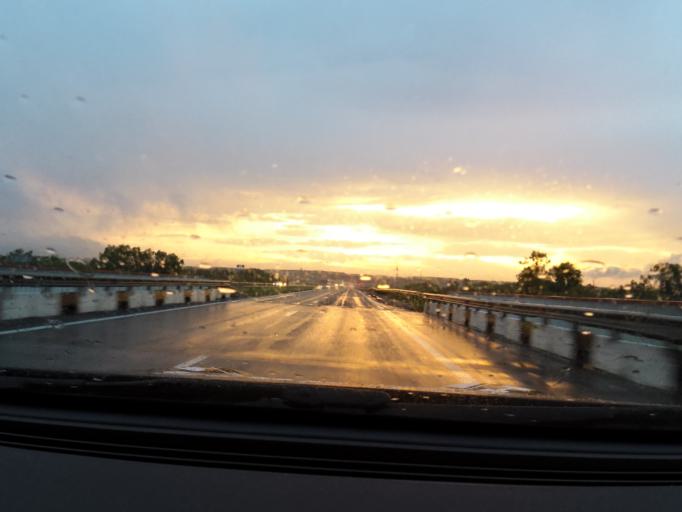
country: RU
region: Tatarstan
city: Yelabuga
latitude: 55.7688
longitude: 52.2165
